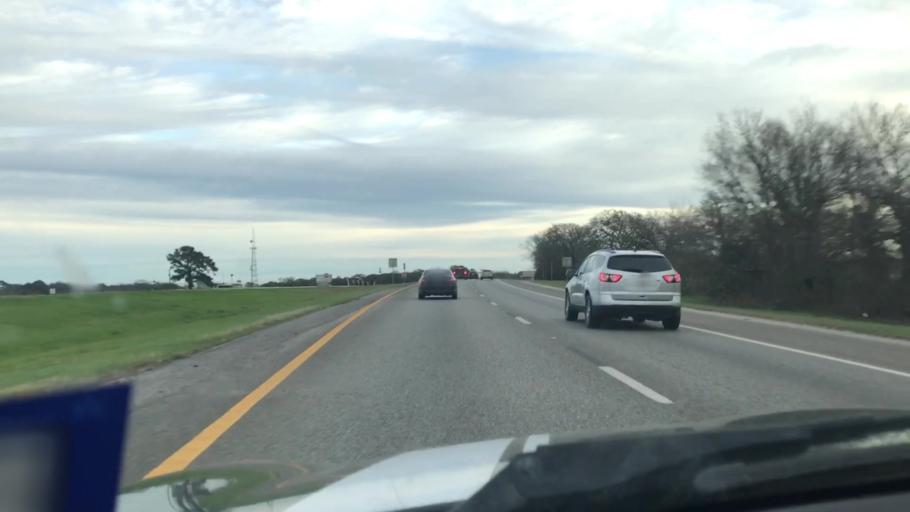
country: US
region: Texas
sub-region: Waller County
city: Hempstead
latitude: 30.1301
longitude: -96.1430
